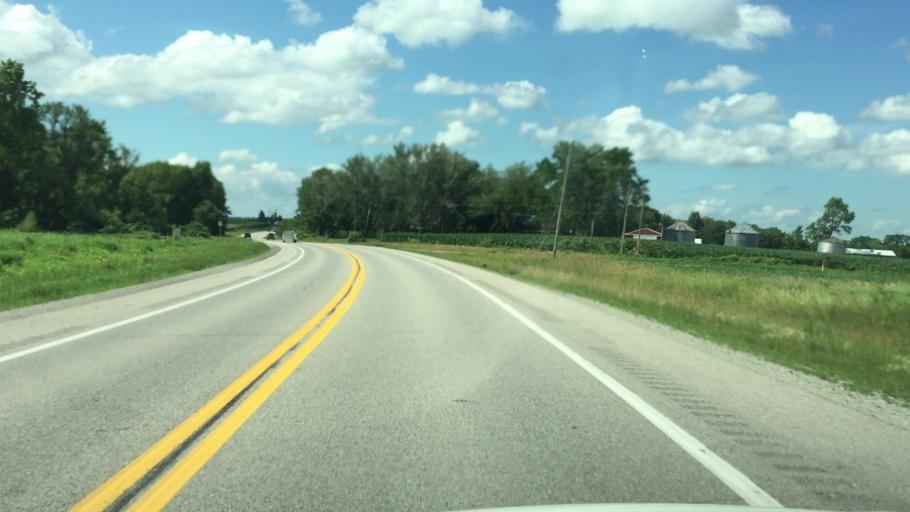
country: US
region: Iowa
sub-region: Johnson County
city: Solon
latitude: 41.7791
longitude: -91.4830
